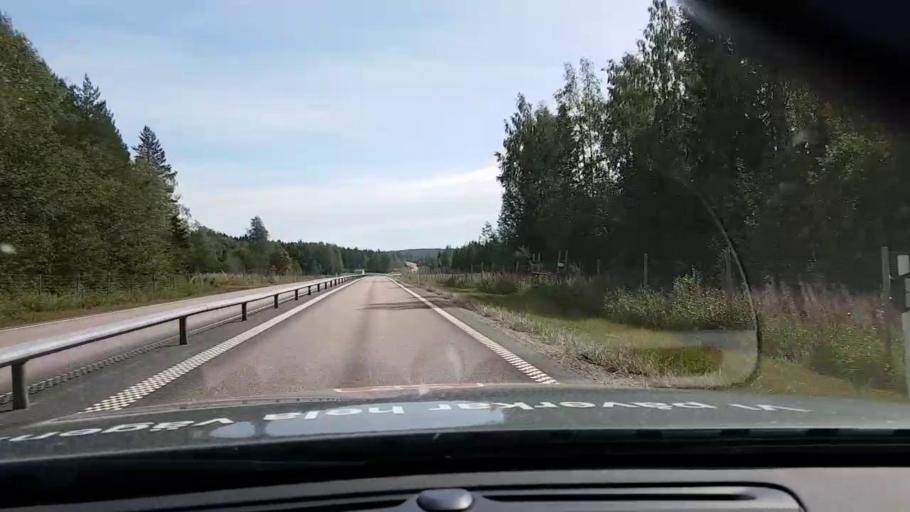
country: SE
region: Vaesternorrland
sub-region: OErnskoeldsviks Kommun
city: Ornskoldsvik
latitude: 63.3041
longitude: 18.8548
